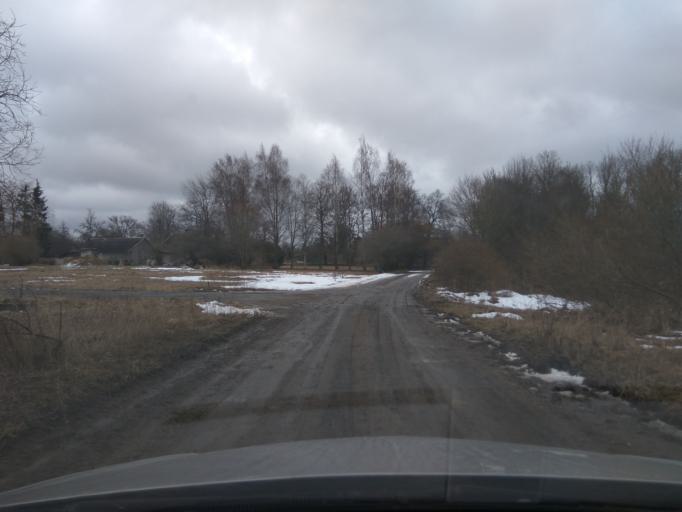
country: LV
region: Ventspils
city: Ventspils
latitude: 57.3336
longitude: 21.6457
